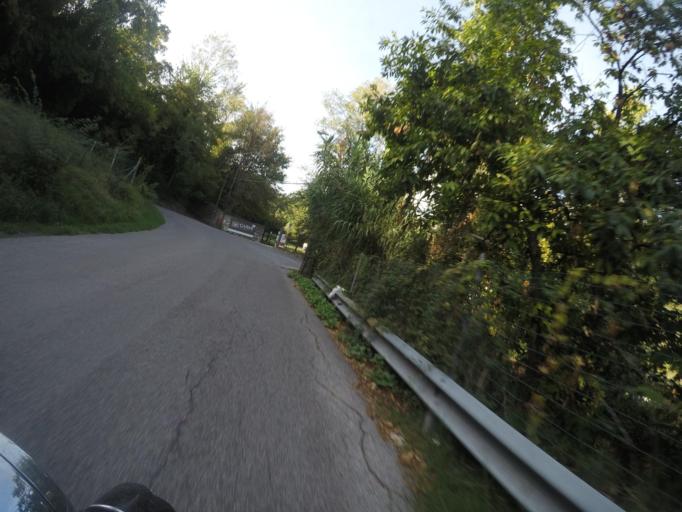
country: IT
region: Tuscany
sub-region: Provincia di Massa-Carrara
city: Carrara
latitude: 44.0839
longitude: 10.0931
